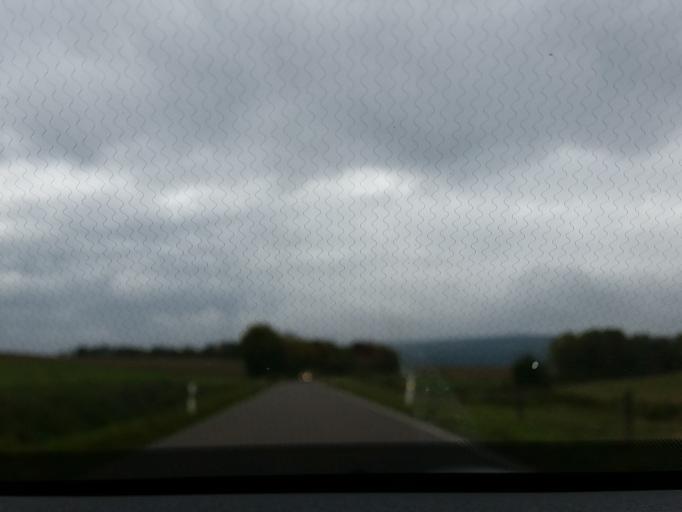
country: DE
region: Saarland
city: Weiskirchen
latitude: 49.5285
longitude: 6.8113
